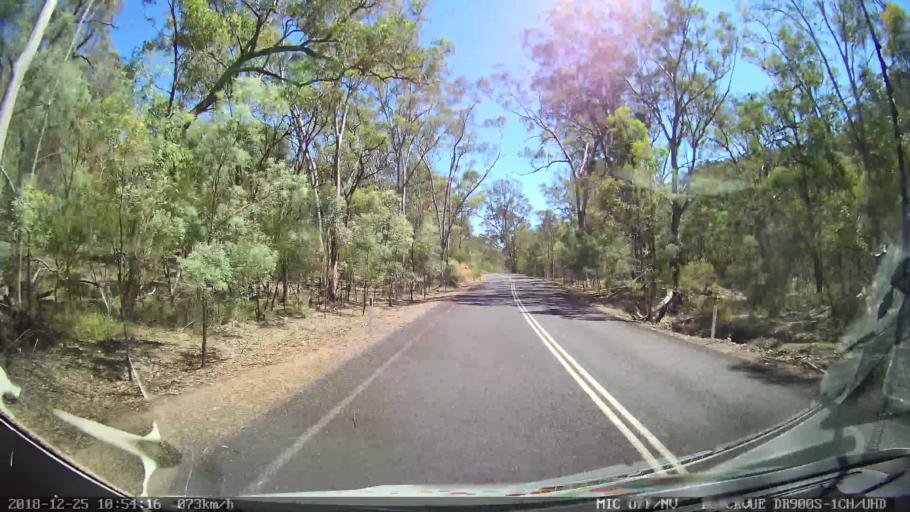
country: AU
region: New South Wales
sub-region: Upper Hunter Shire
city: Merriwa
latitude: -32.4117
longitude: 150.2728
